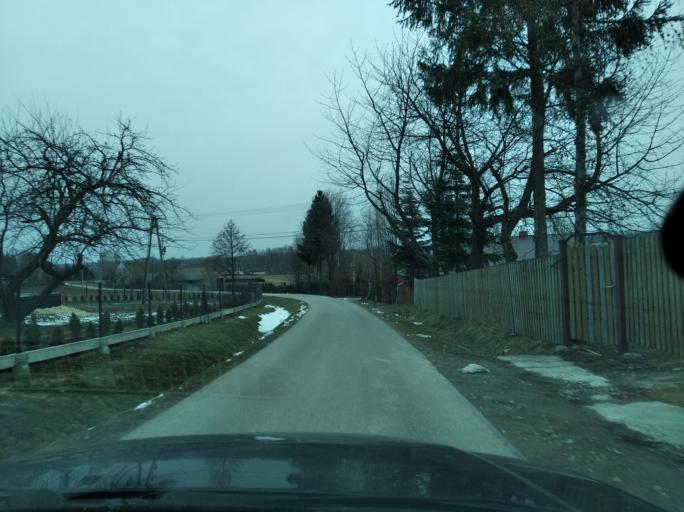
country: PL
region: Subcarpathian Voivodeship
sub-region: Powiat rzeszowski
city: Chmielnik
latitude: 49.9899
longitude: 22.1462
